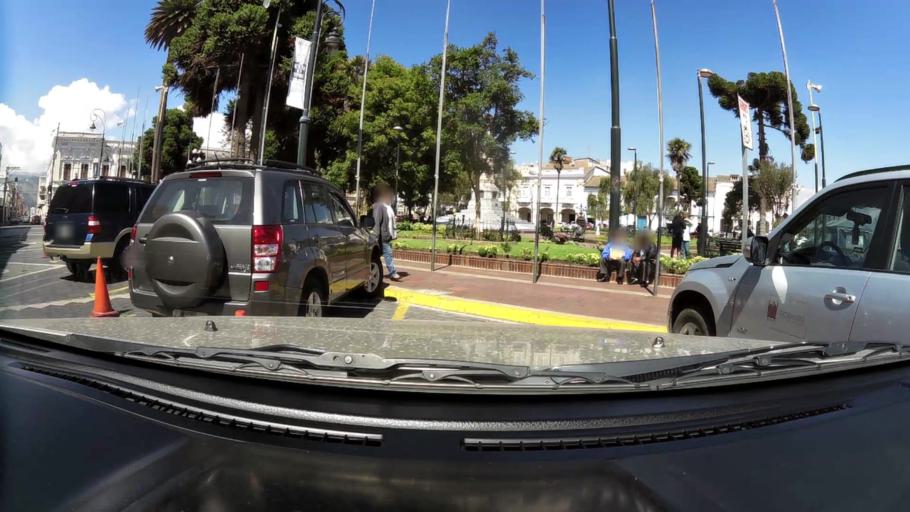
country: EC
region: Chimborazo
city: Riobamba
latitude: -1.6728
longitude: -78.6479
